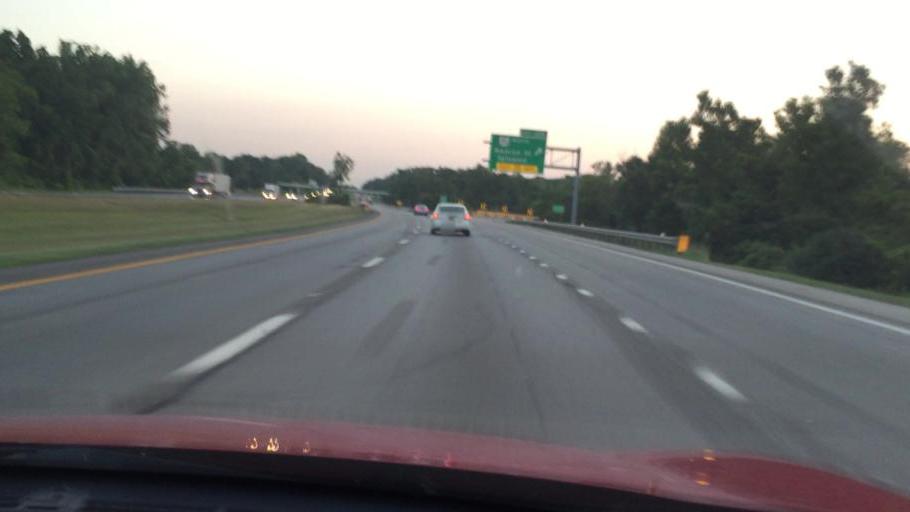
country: US
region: Ohio
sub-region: Lucas County
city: Sylvania
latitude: 41.7097
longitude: -83.6880
